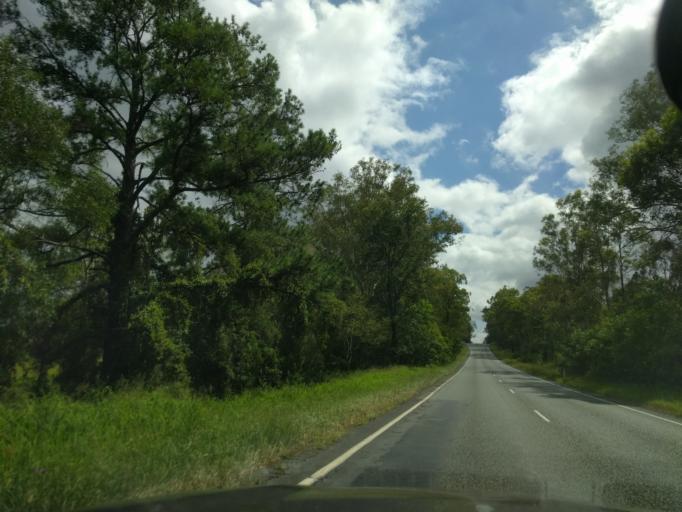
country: AU
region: Queensland
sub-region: Logan
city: Cedar Vale
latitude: -27.8564
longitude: 153.0075
